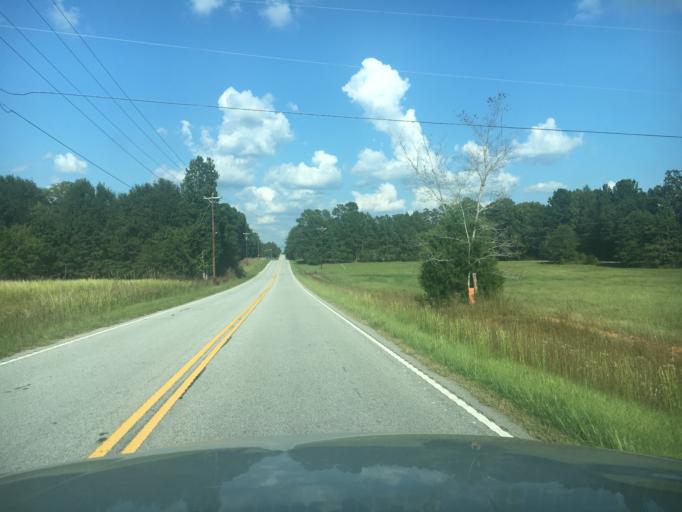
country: US
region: South Carolina
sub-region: Greenwood County
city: Ware Shoals
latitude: 34.5132
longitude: -82.2036
